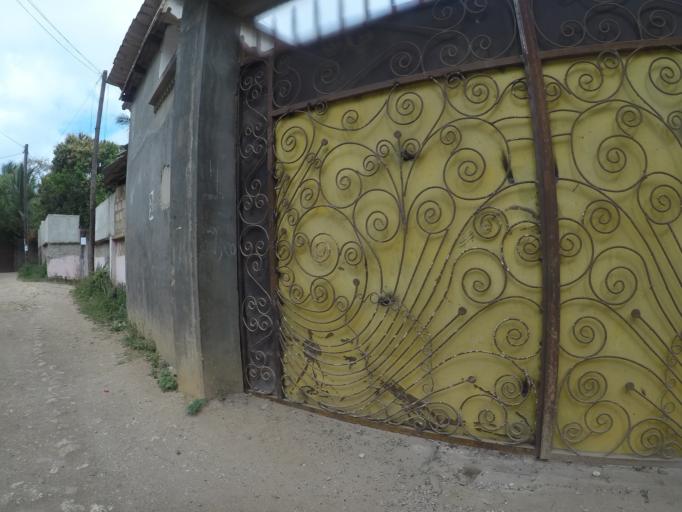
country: TZ
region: Zanzibar Urban/West
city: Zanzibar
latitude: -6.2123
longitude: 39.2173
